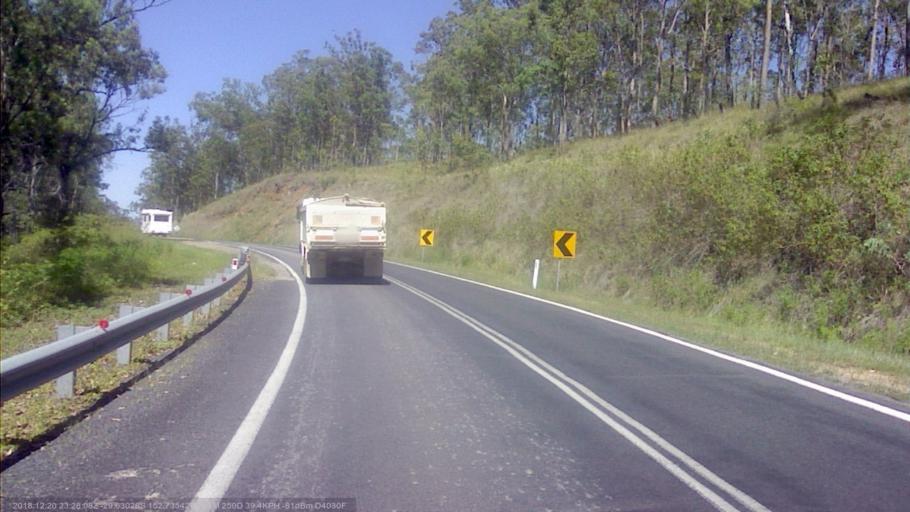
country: AU
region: New South Wales
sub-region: Clarence Valley
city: South Grafton
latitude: -29.6303
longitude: 152.7354
